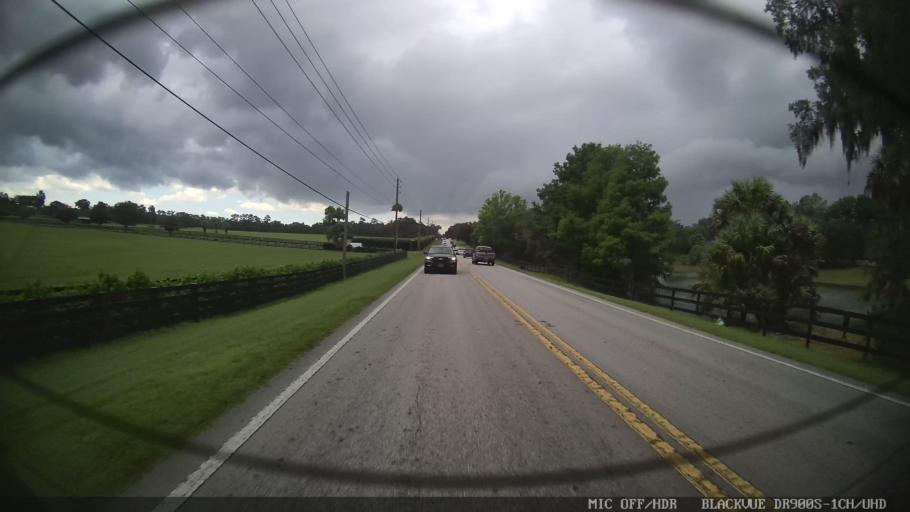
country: US
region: Florida
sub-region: Marion County
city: Ocala
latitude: 29.1412
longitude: -82.1689
